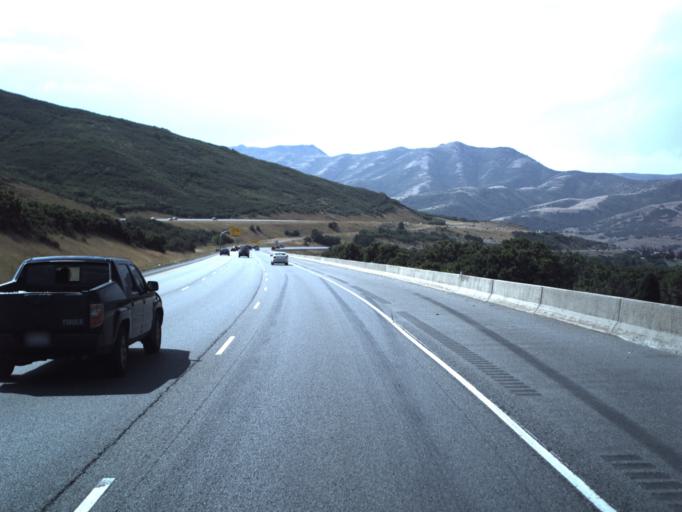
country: US
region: Utah
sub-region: Summit County
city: Summit Park
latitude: 40.7435
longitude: -111.6812
